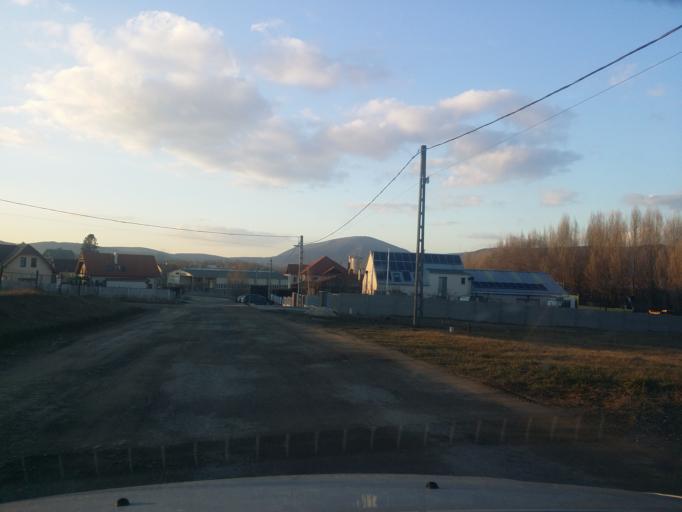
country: HU
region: Pest
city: Pilisvorosvar
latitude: 47.6158
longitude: 18.9284
